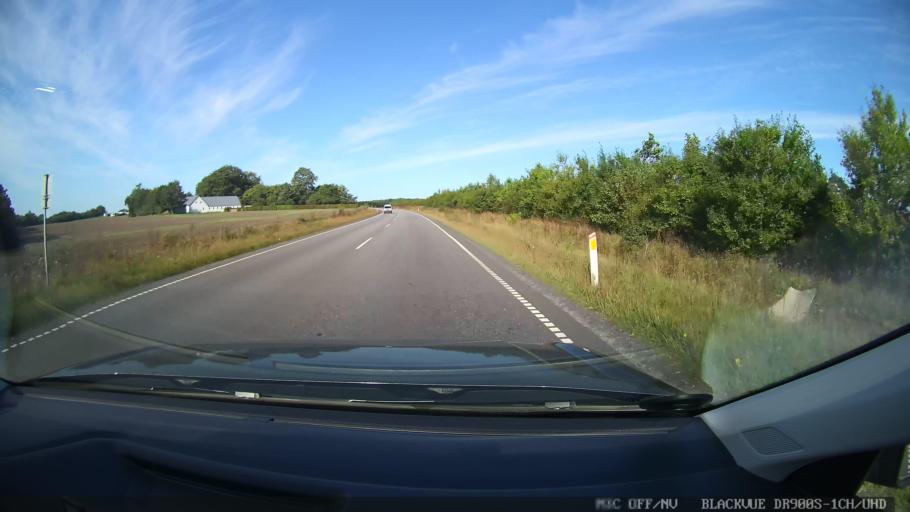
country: DK
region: North Denmark
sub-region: Mariagerfjord Kommune
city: Hobro
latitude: 56.6643
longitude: 9.7744
